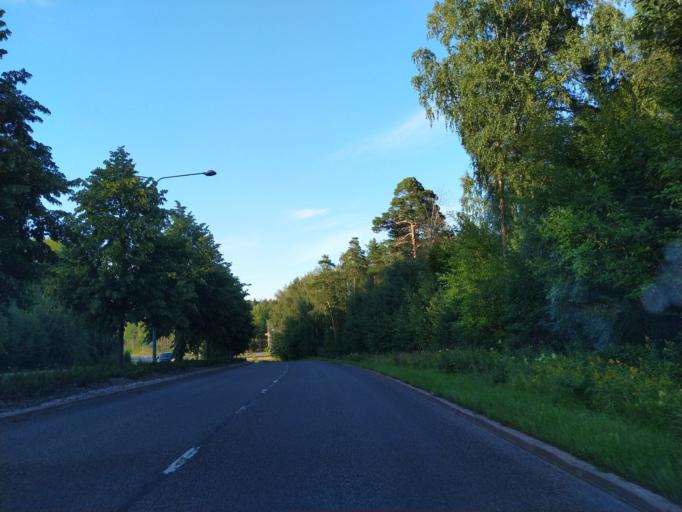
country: FI
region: Varsinais-Suomi
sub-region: Turku
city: Turku
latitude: 60.4285
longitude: 22.3166
